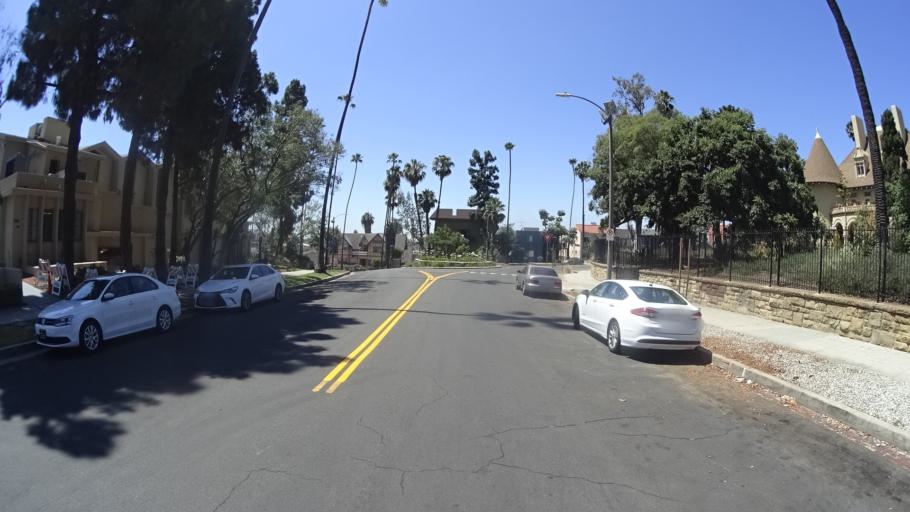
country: US
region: California
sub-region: Los Angeles County
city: View Park-Windsor Hills
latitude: 34.0346
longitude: -118.3066
